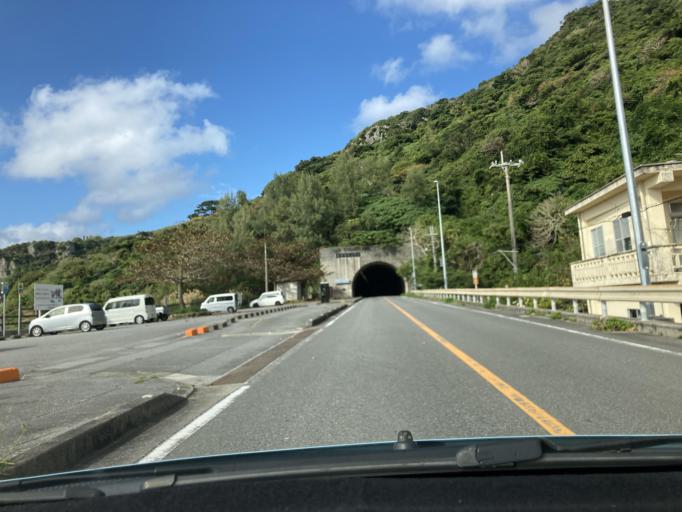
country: JP
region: Okinawa
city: Nago
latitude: 26.8501
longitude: 128.2537
